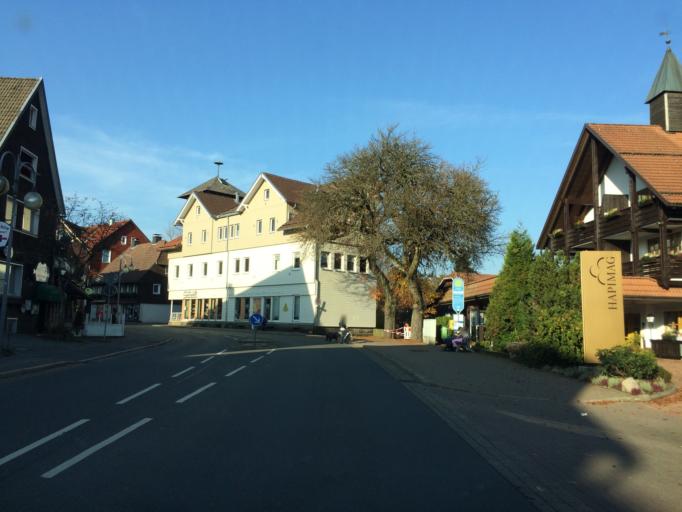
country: DE
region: Lower Saxony
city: Braunlage
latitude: 51.7236
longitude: 10.6122
